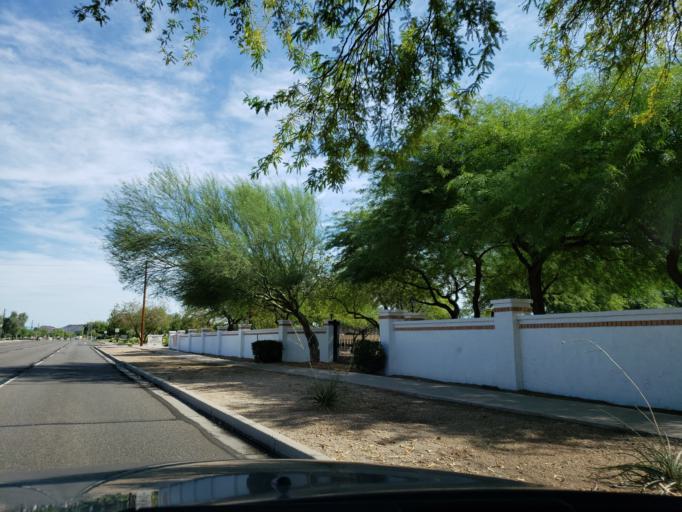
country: US
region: Arizona
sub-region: Maricopa County
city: Peoria
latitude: 33.6342
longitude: -112.1511
